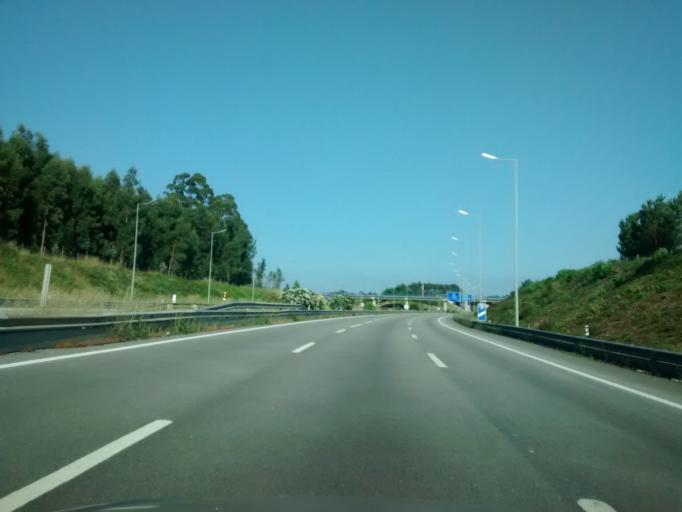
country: PT
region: Aveiro
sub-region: Estarreja
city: Salreu
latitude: 40.6908
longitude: -8.5498
